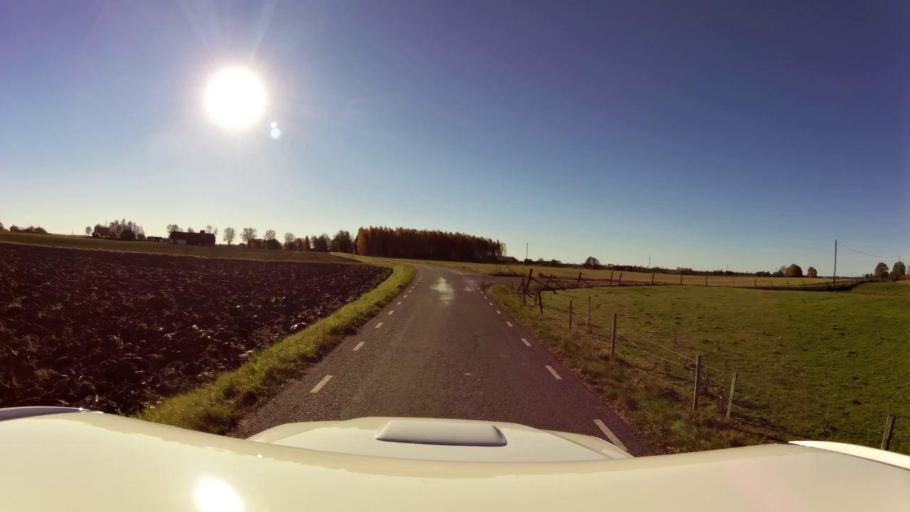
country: SE
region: OEstergoetland
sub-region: Linkopings Kommun
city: Ljungsbro
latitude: 58.4875
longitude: 15.4177
